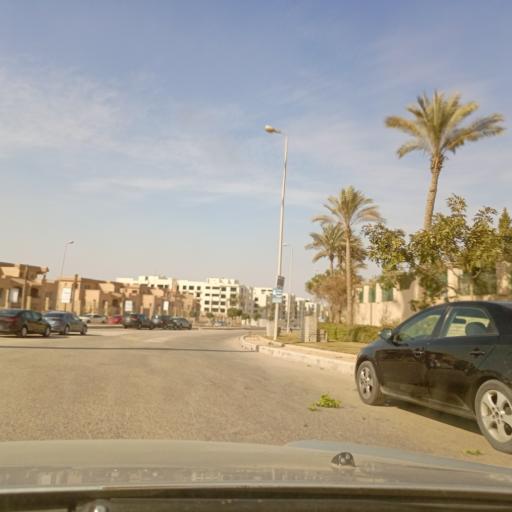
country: EG
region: Muhafazat al Qalyubiyah
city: Al Khankah
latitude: 30.0296
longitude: 31.4854
